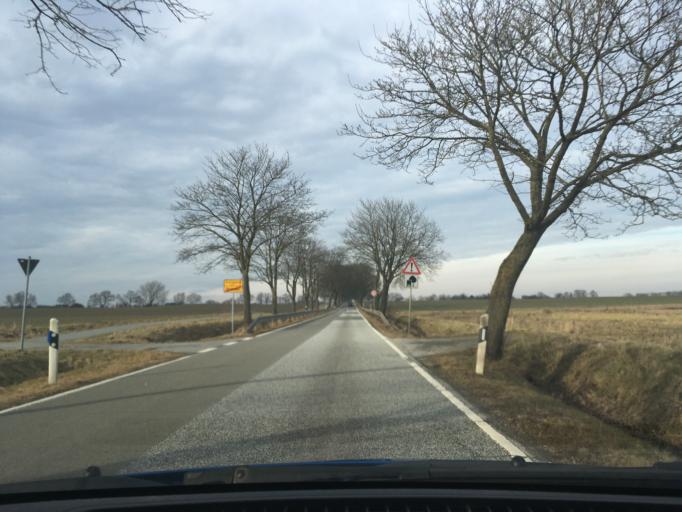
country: DE
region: Mecklenburg-Vorpommern
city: Stralendorf
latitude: 53.5790
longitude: 11.3065
